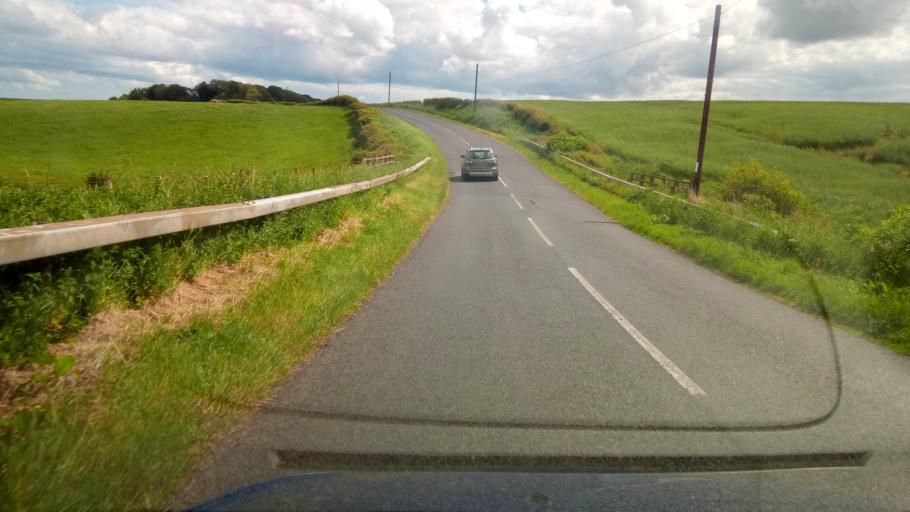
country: GB
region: Scotland
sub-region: The Scottish Borders
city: Coldstream
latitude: 55.6052
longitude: -2.3159
